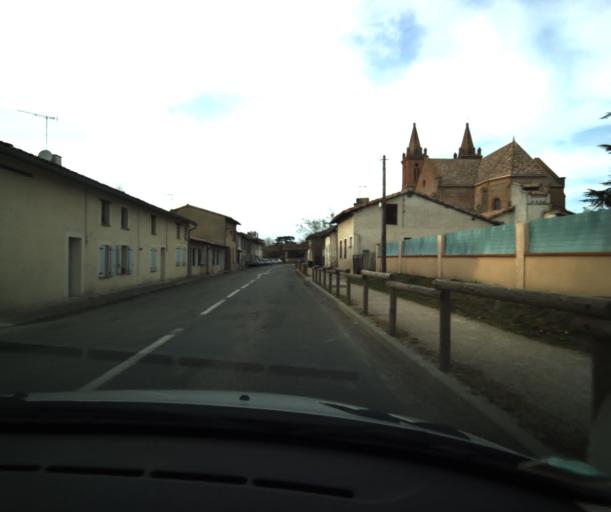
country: FR
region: Midi-Pyrenees
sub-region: Departement du Tarn-et-Garonne
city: Montech
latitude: 43.9532
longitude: 1.2315
